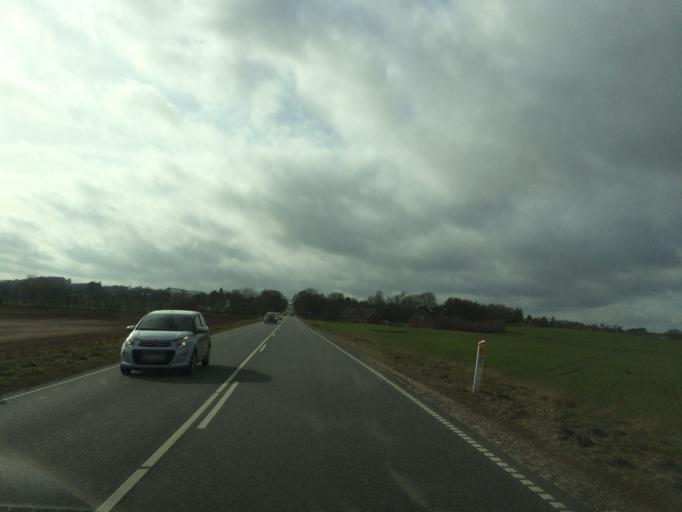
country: DK
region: Central Jutland
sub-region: Randers Kommune
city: Langa
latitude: 56.4929
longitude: 9.8523
